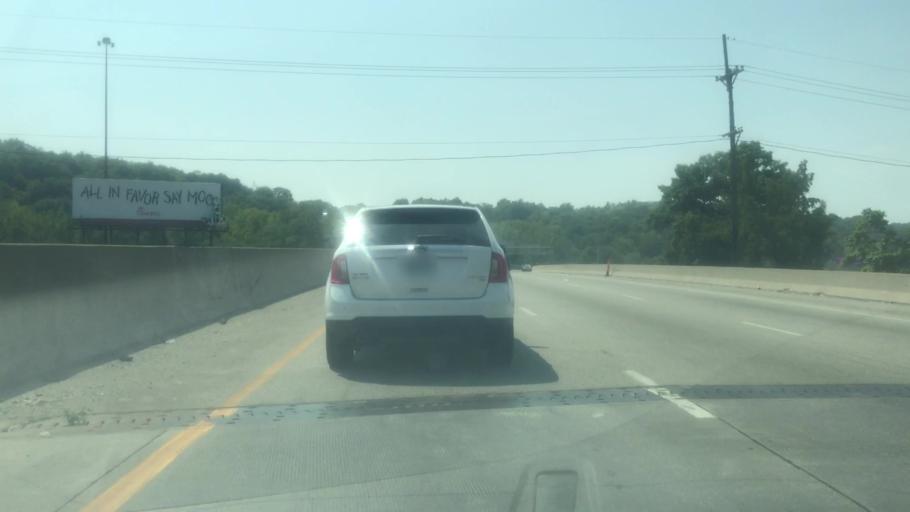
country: US
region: Kansas
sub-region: Johnson County
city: Westwood
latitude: 39.0590
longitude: -94.6282
